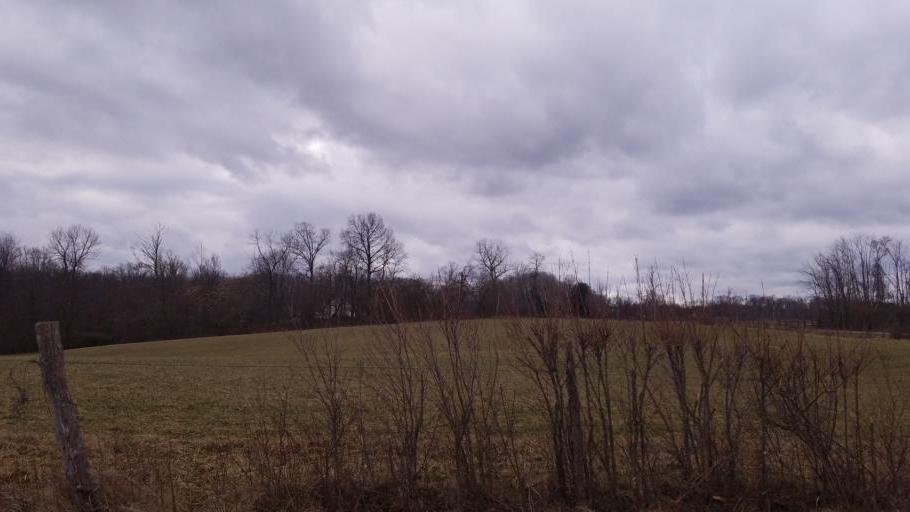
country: US
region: Ohio
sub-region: Knox County
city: Fredericktown
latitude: 40.3925
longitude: -82.6130
